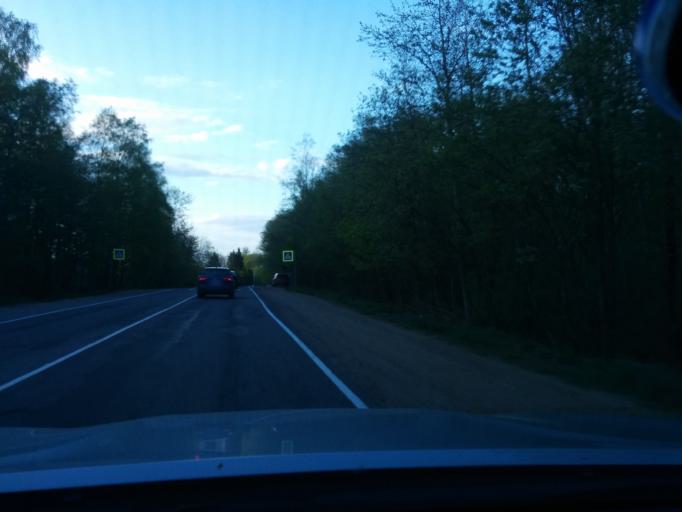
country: RU
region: Leningrad
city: Verkhniye Osel'ki
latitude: 60.2406
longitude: 30.4413
